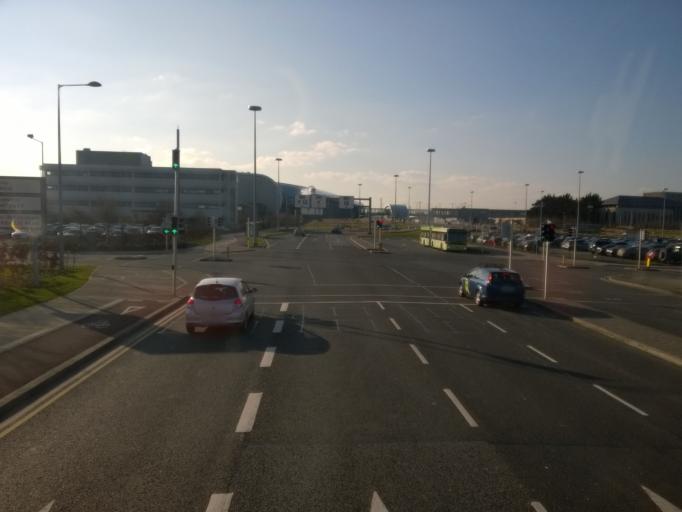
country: IE
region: Leinster
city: Beaumont
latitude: 53.4242
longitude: -6.2336
